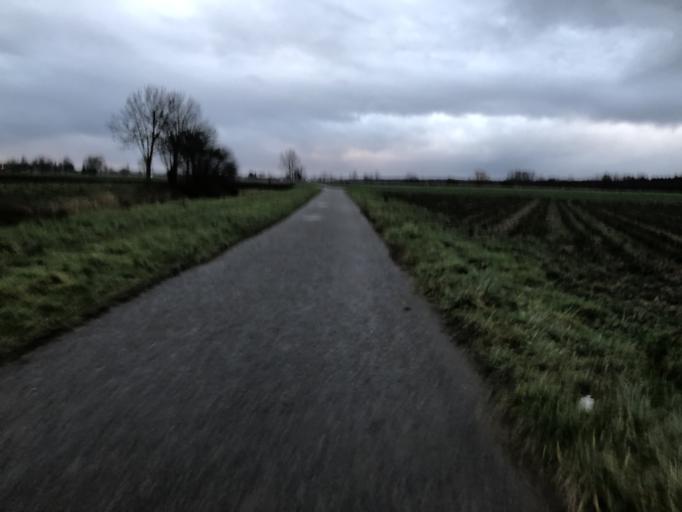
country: DE
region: Baden-Wuerttemberg
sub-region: Karlsruhe Region
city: Reilingen
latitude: 49.2984
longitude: 8.5771
